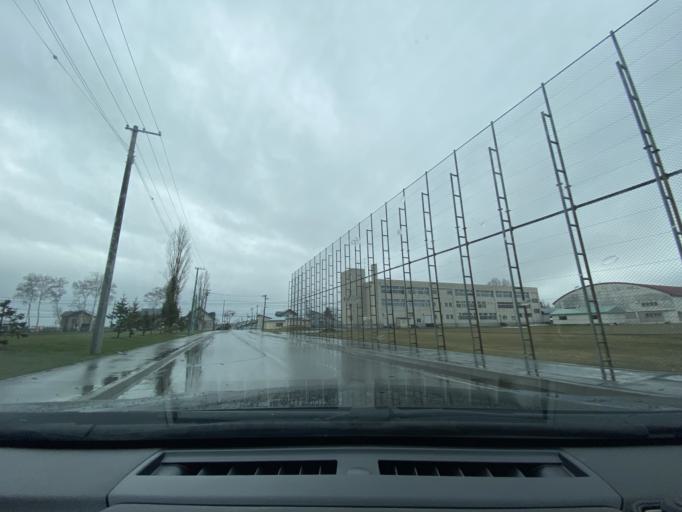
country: JP
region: Hokkaido
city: Fukagawa
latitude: 43.8090
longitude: 141.9257
